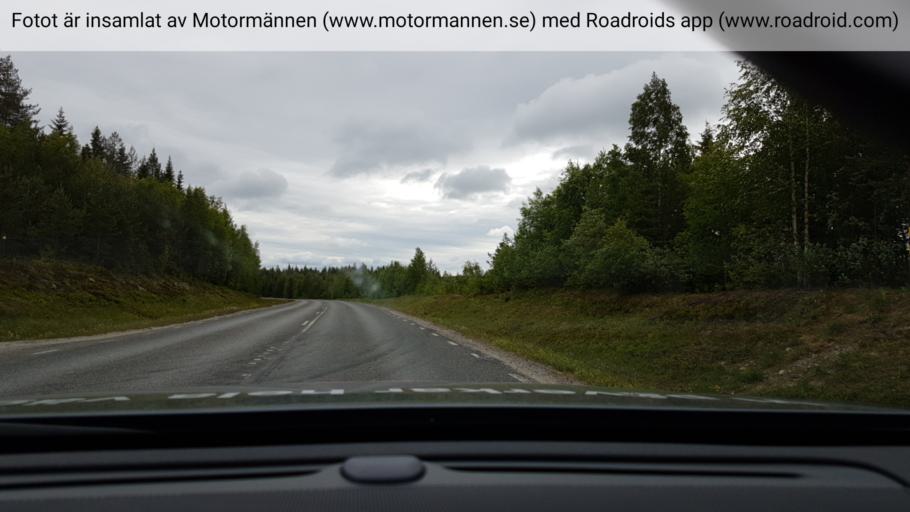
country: SE
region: Vaesterbotten
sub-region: Lycksele Kommun
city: Lycksele
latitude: 64.5152
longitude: 18.4177
